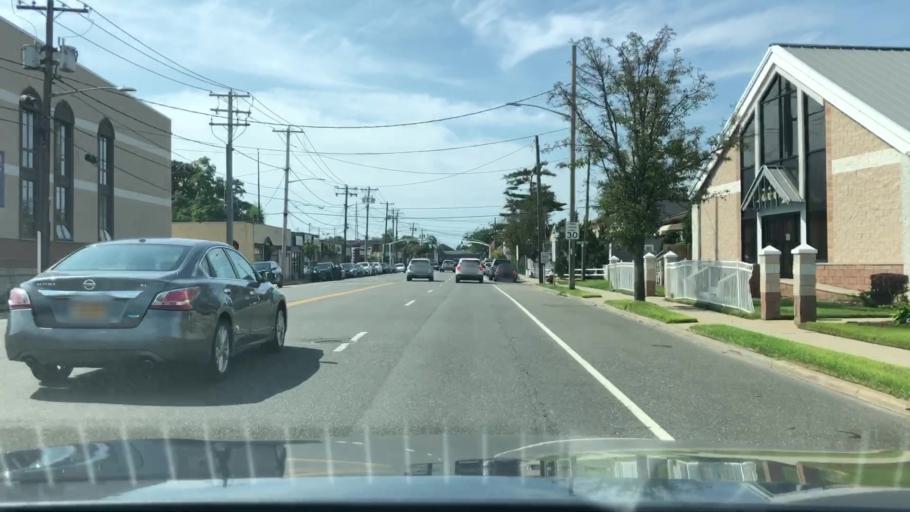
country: US
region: New York
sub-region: Nassau County
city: Baldwin
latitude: 40.6602
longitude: -73.6081
